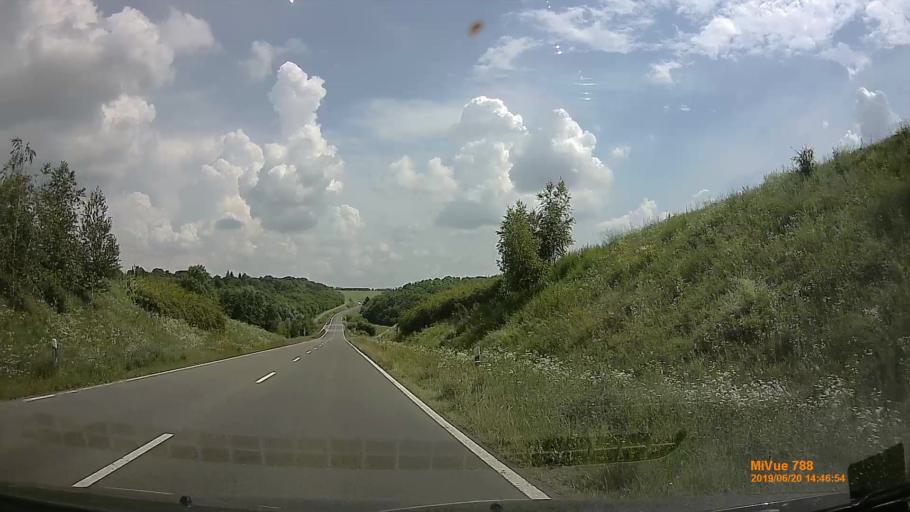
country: HU
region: Baranya
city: Kozarmisleny
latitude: 46.0293
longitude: 18.2765
